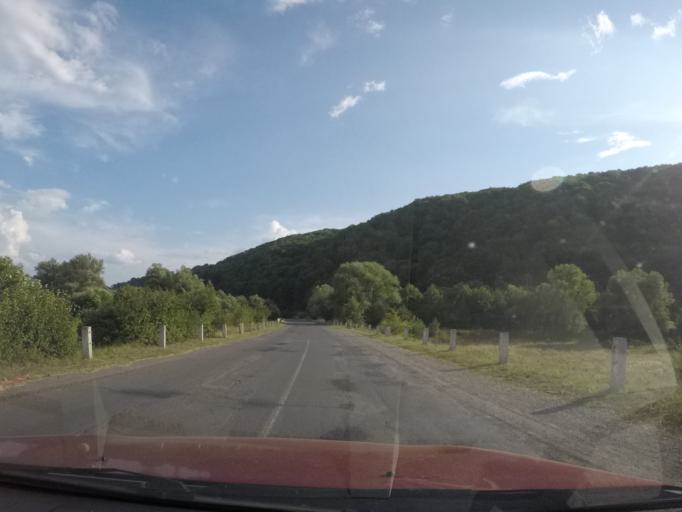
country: UA
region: Zakarpattia
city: Velykyi Bereznyi
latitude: 48.9238
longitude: 22.4562
